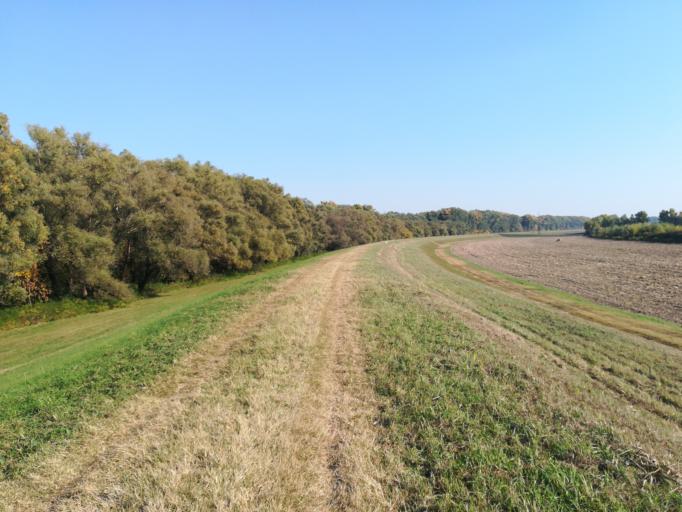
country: HU
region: Bacs-Kiskun
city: Tiszakecske
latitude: 46.9379
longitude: 20.1385
